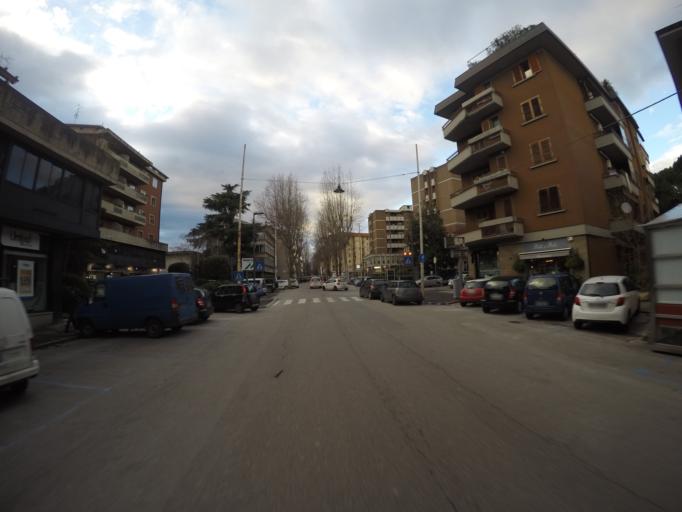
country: IT
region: Tuscany
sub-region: Provincia di Prato
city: Prato
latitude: 43.8711
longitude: 11.1102
